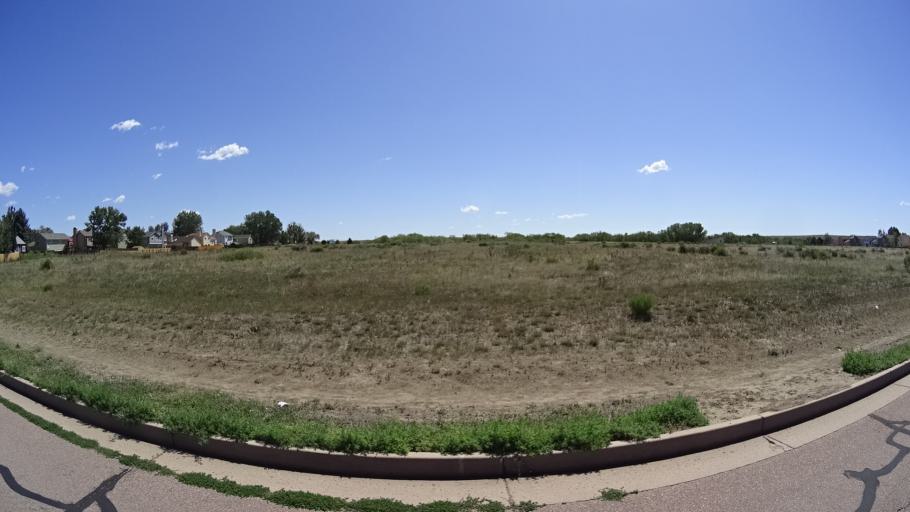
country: US
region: Colorado
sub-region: El Paso County
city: Security-Widefield
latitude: 38.7701
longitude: -104.6526
